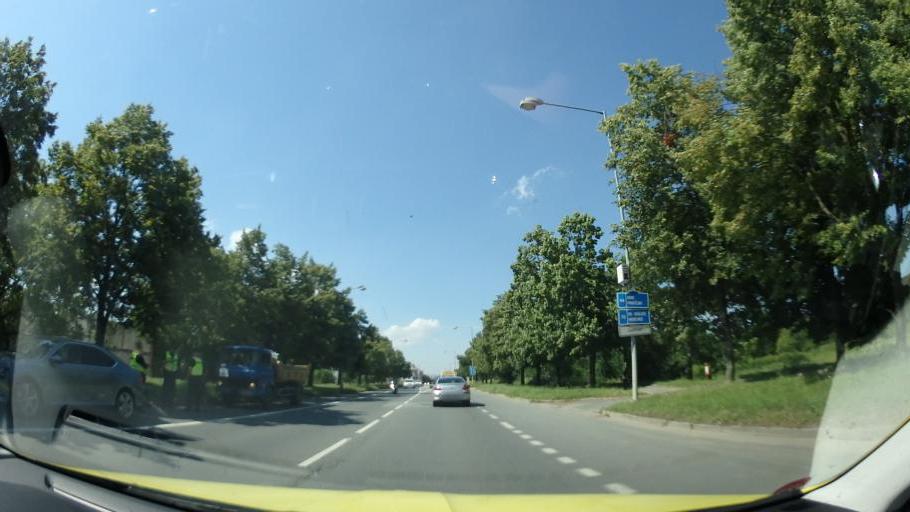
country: CZ
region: Olomoucky
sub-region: Okres Olomouc
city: Olomouc
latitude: 49.5690
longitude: 17.2608
